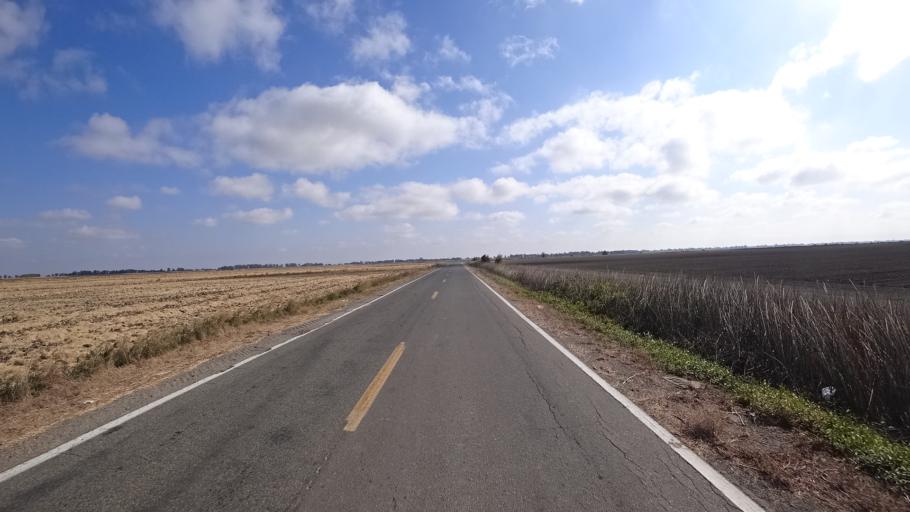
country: US
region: California
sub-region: Yolo County
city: Woodland
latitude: 38.8461
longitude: -121.7600
